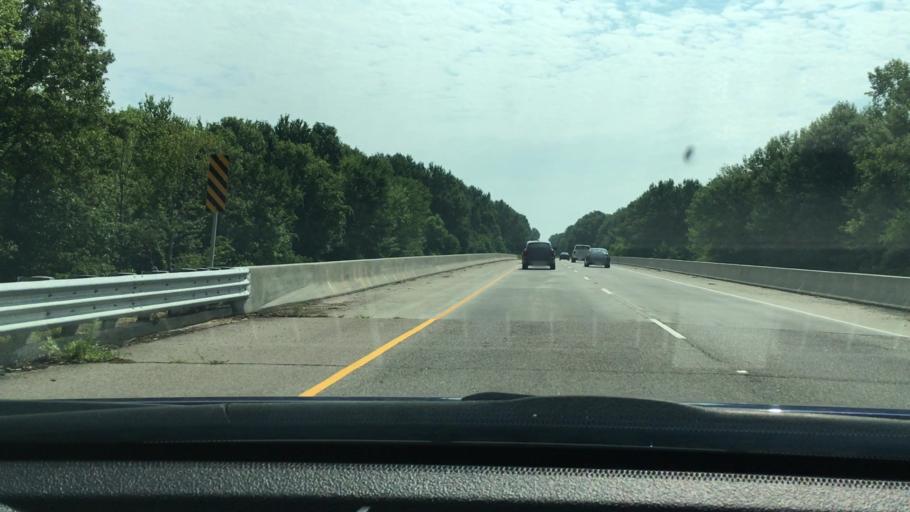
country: US
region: South Carolina
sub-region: Sumter County
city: Stateburg
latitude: 33.9502
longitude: -80.5943
